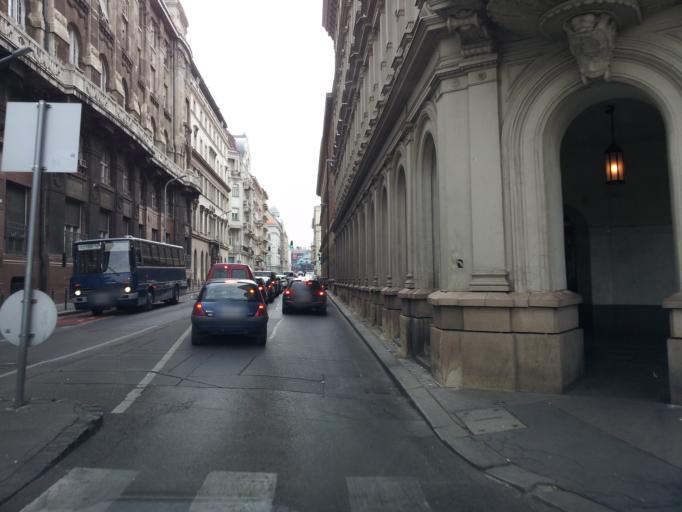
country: HU
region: Budapest
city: Budapest
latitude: 47.4986
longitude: 19.0484
